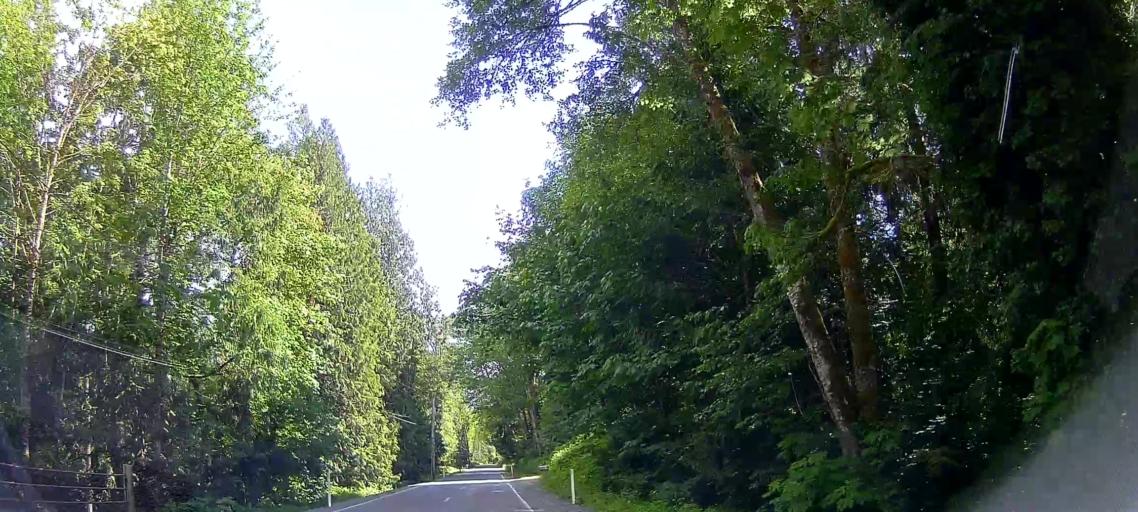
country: US
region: Washington
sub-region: Skagit County
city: Sedro-Woolley
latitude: 48.5498
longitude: -122.2131
